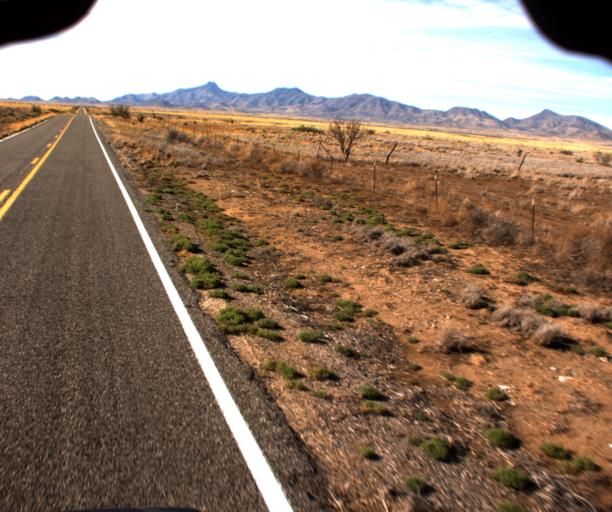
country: US
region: Arizona
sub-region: Cochise County
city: Willcox
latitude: 32.0733
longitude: -109.5140
